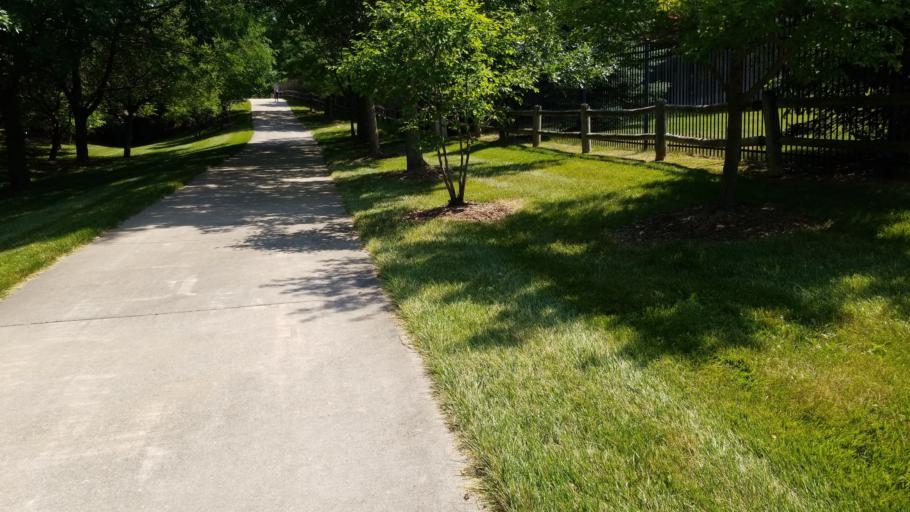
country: US
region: Nebraska
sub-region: Douglas County
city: Elkhorn
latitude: 41.2834
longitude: -96.1629
